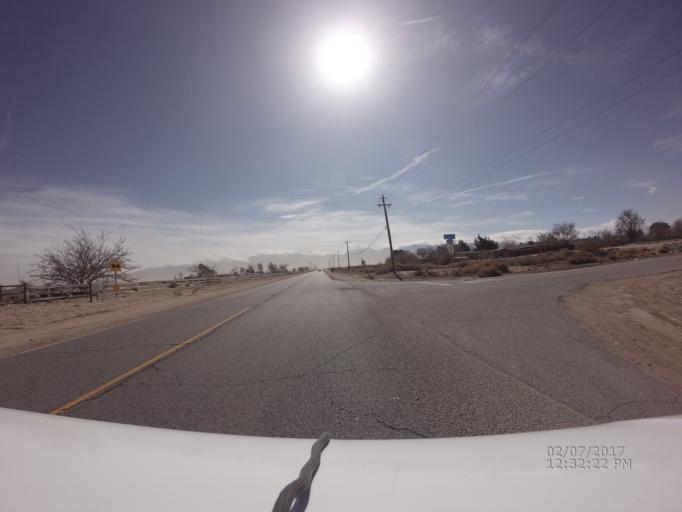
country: US
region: California
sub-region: Los Angeles County
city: Lake Los Angeles
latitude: 34.5946
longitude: -117.8268
